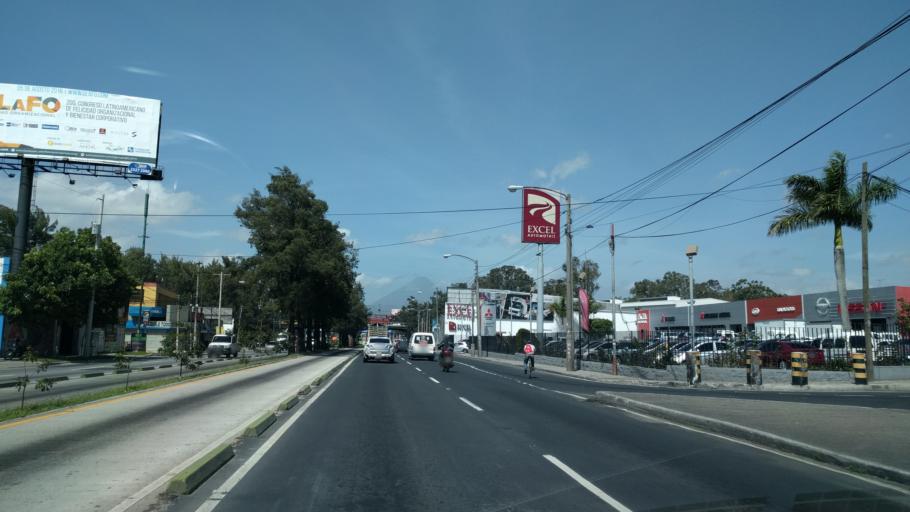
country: GT
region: Guatemala
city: Guatemala City
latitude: 14.5982
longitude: -90.5534
